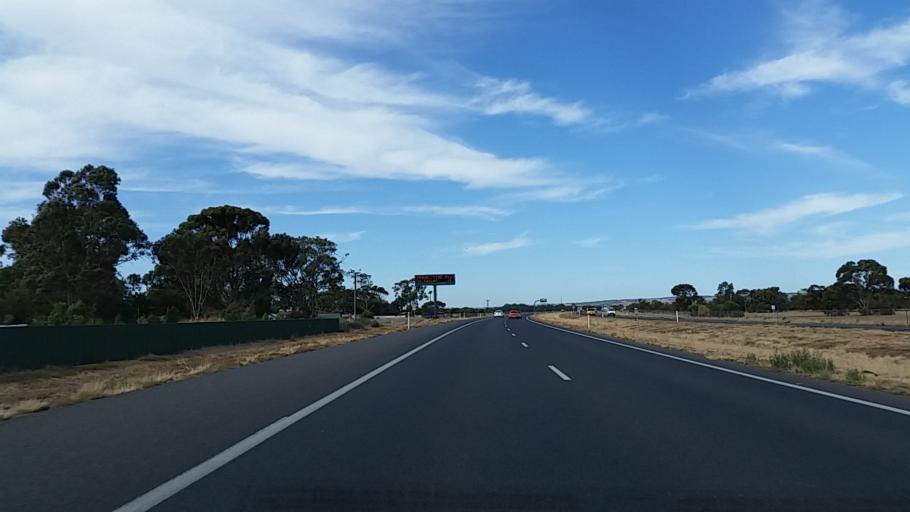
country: AU
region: South Australia
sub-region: Playford
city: Virginia
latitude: -34.6806
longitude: 138.6082
